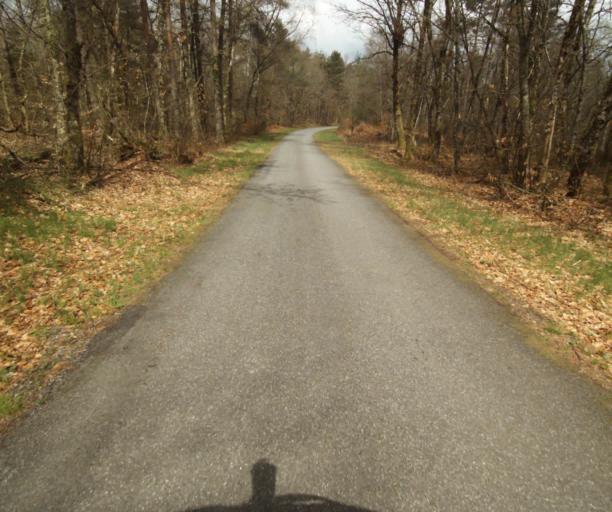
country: FR
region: Limousin
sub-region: Departement de la Correze
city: Correze
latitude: 45.3231
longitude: 1.8947
